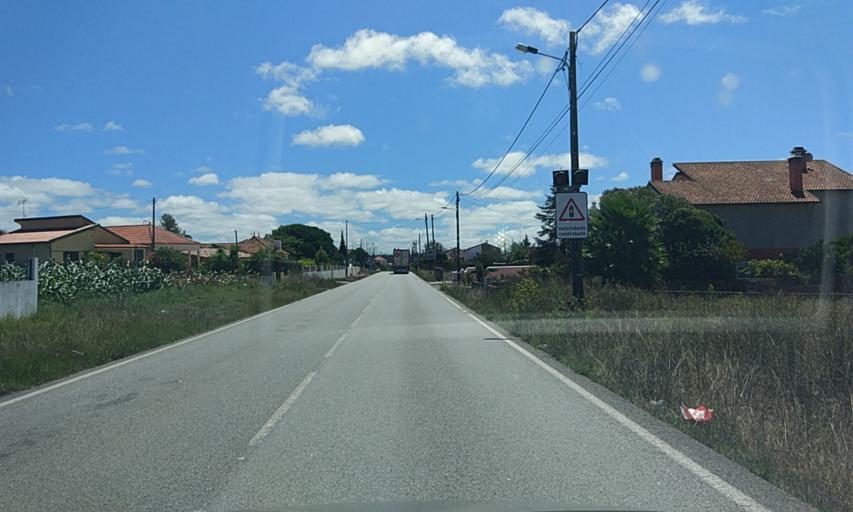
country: PT
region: Coimbra
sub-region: Mira
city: Mira
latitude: 40.4161
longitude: -8.7362
